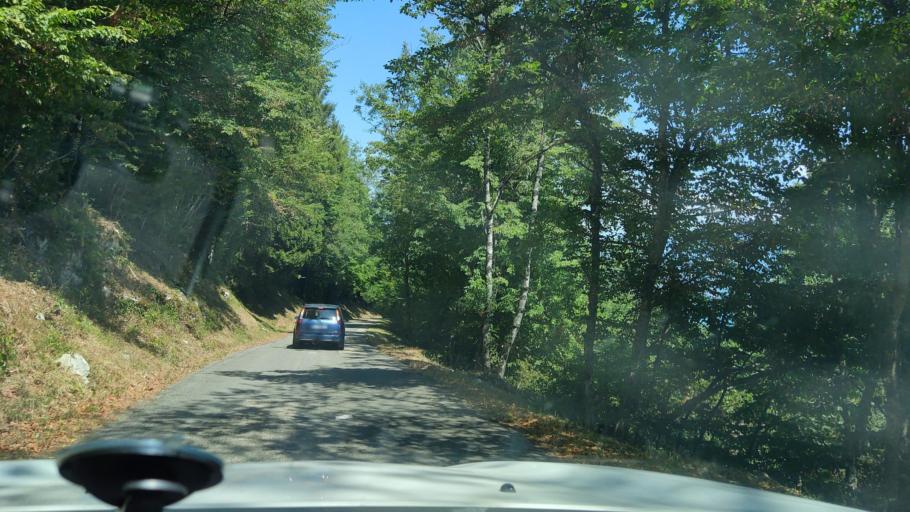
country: FR
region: Rhone-Alpes
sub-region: Departement de la Savoie
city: Le Bourget-du-Lac
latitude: 45.6485
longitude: 5.8363
